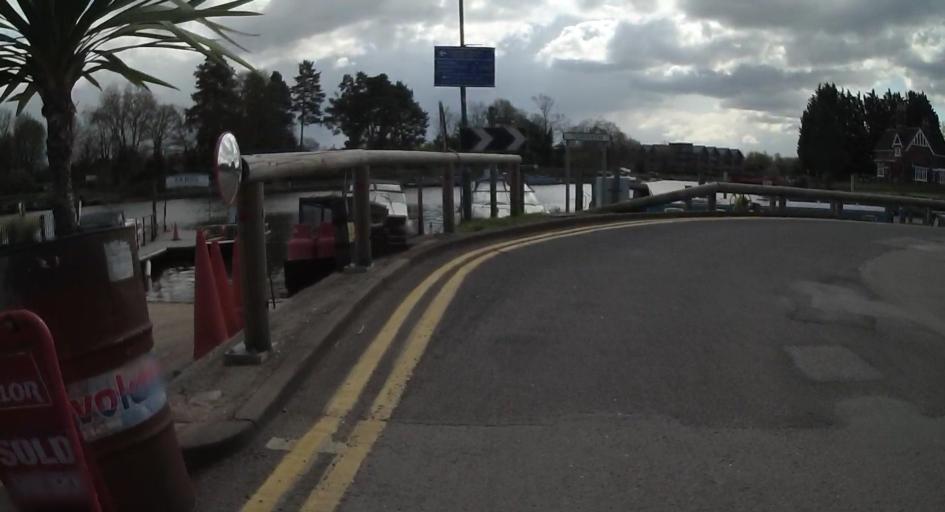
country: GB
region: England
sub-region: Surrey
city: Weybridge
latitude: 51.3828
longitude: -0.4572
